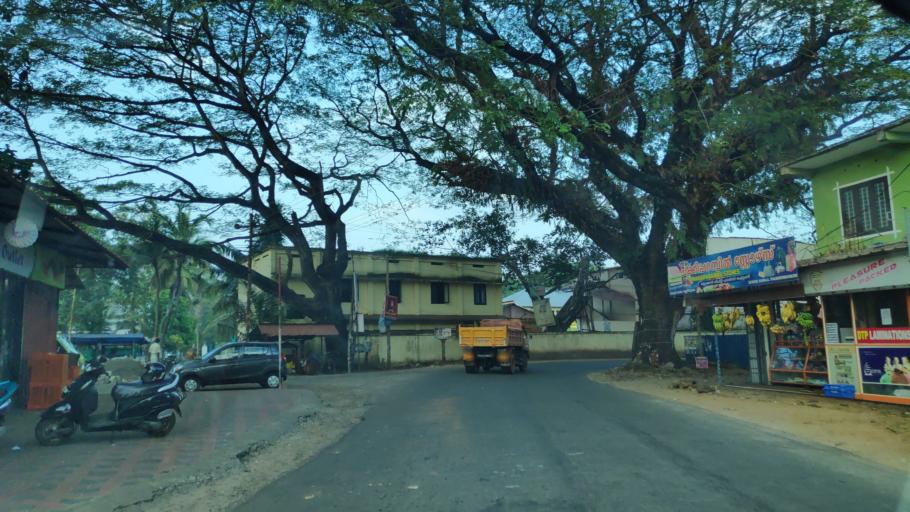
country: IN
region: Kerala
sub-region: Alappuzha
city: Shertallai
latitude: 9.6636
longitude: 76.3829
